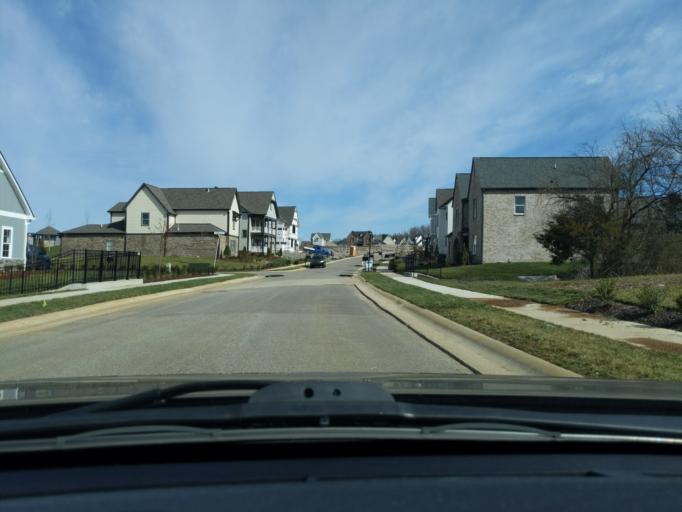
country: US
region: Tennessee
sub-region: Wilson County
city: Mount Juliet
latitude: 36.2100
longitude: -86.4899
